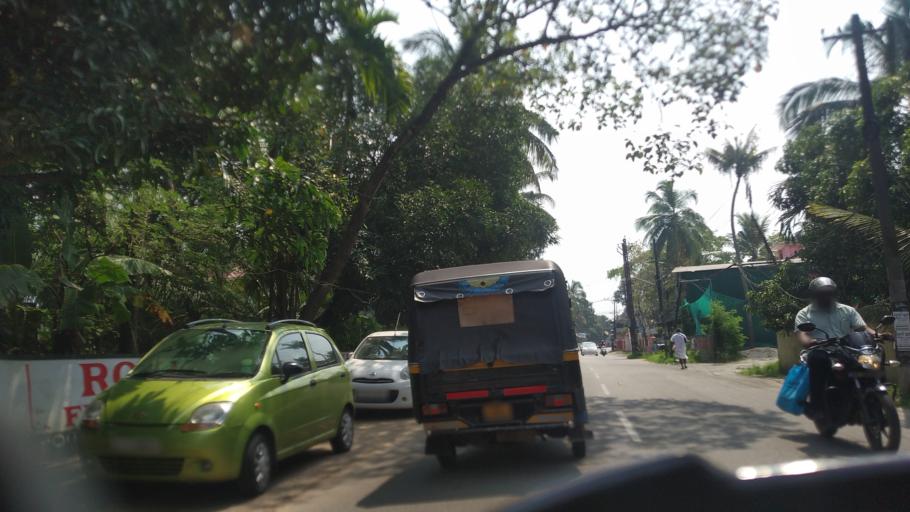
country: IN
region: Kerala
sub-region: Ernakulam
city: Elur
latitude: 10.0116
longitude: 76.2294
